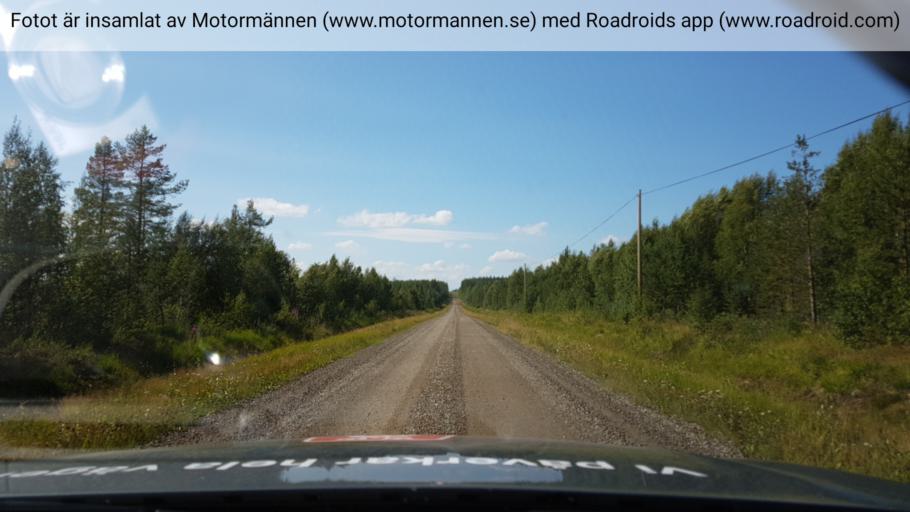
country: SE
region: Vaesterbotten
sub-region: Dorotea Kommun
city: Dorotea
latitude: 64.0898
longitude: 16.5256
